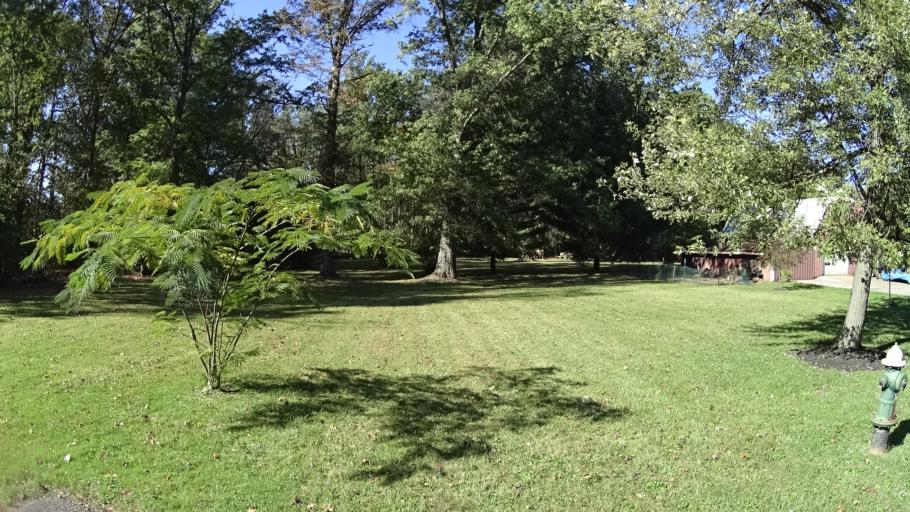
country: US
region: Ohio
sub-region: Lorain County
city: Lorain
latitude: 41.4233
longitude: -82.1646
